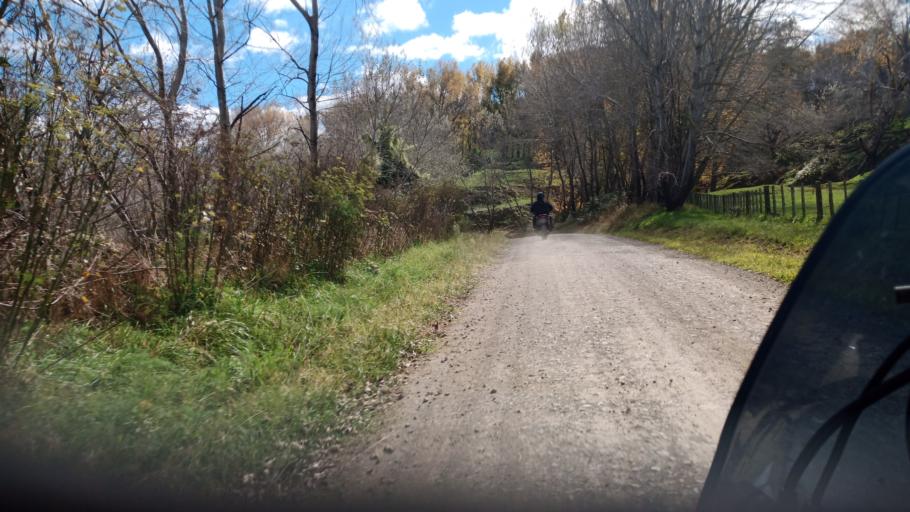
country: NZ
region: Gisborne
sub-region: Gisborne District
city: Gisborne
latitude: -38.4247
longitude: 177.7233
